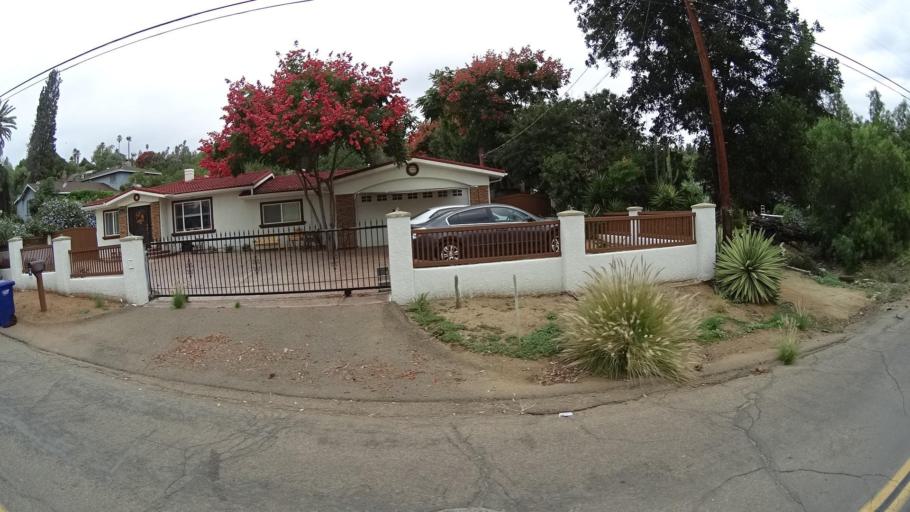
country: US
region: California
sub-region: San Diego County
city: Spring Valley
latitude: 32.7516
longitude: -116.9895
